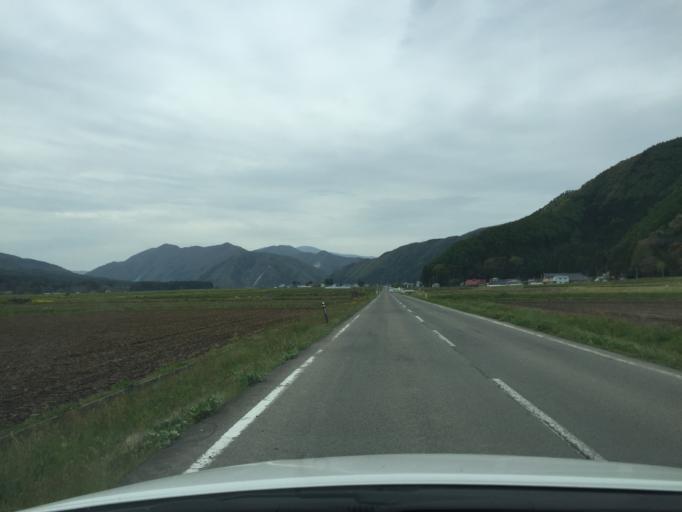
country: JP
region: Fukushima
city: Inawashiro
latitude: 37.5699
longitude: 140.1350
